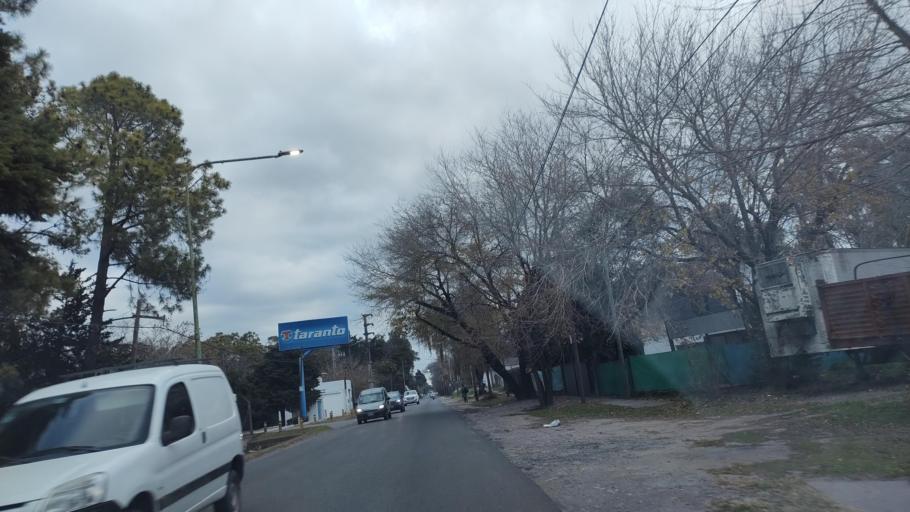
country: AR
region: Buenos Aires
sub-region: Partido de La Plata
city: La Plata
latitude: -34.8637
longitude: -58.0911
